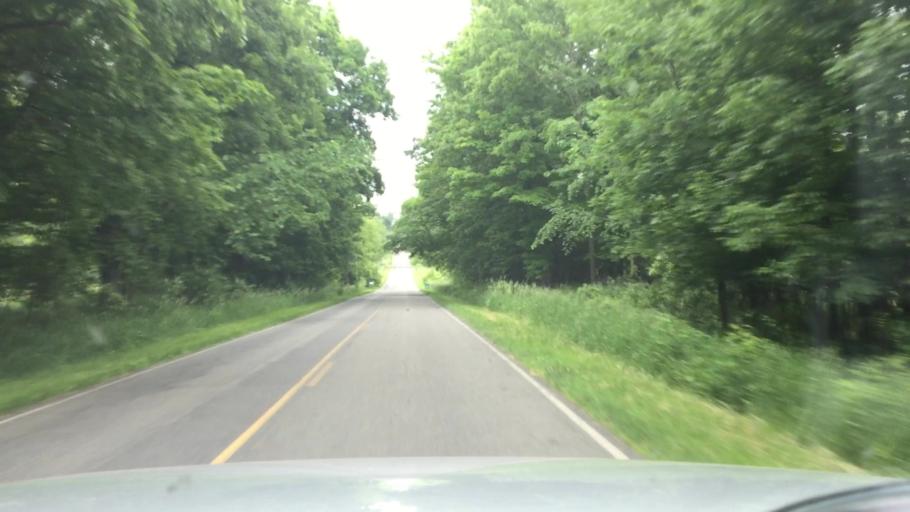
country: US
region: Michigan
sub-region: Shiawassee County
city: Durand
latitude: 42.7887
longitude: -84.0018
